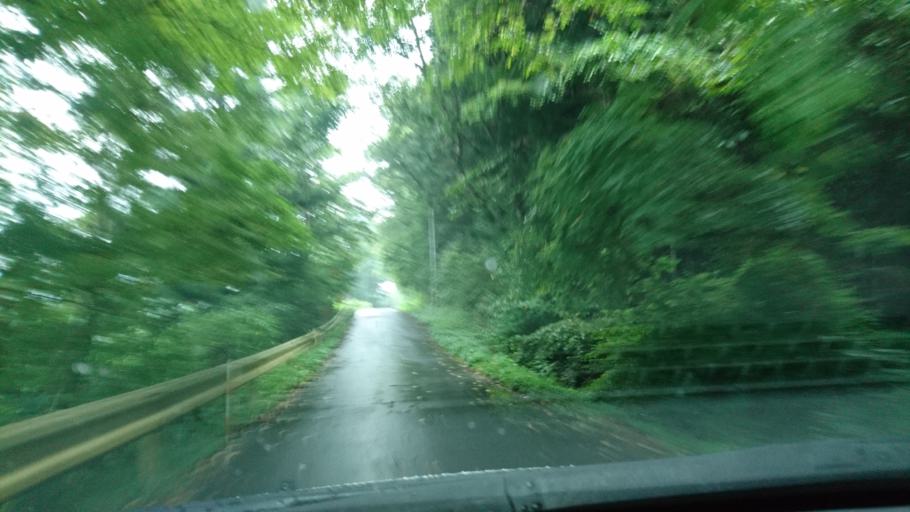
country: JP
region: Iwate
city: Ichinoseki
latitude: 38.8785
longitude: 141.2580
